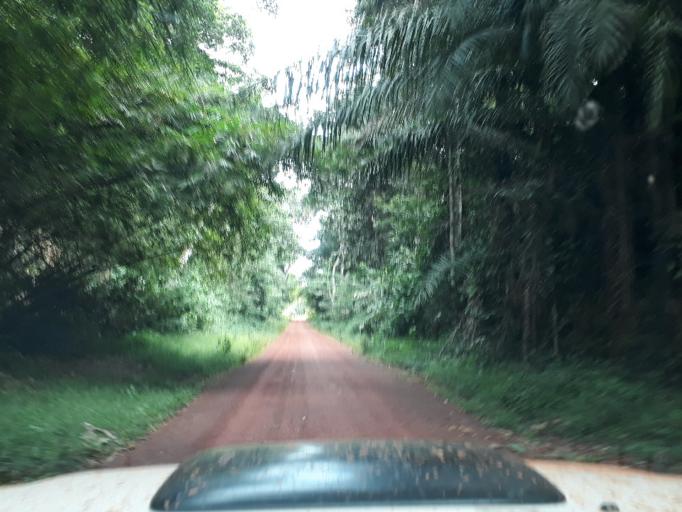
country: CD
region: Eastern Province
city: Buta
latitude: 2.2937
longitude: 25.0511
